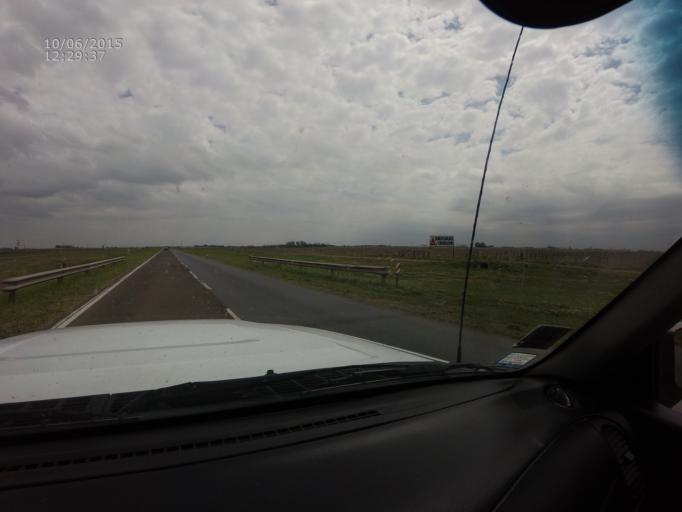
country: AR
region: Santa Fe
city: Carcarana
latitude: -32.8916
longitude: -61.0844
